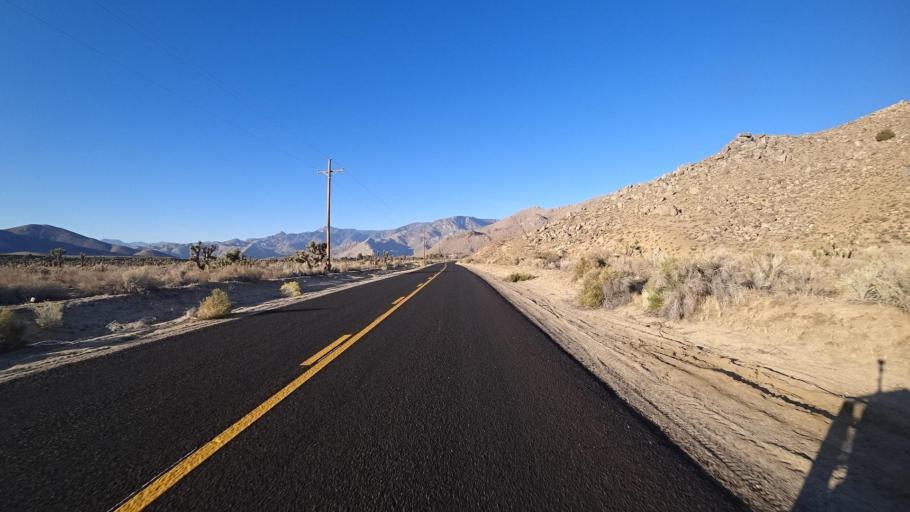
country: US
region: California
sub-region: Kern County
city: Weldon
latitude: 35.6229
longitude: -118.2436
